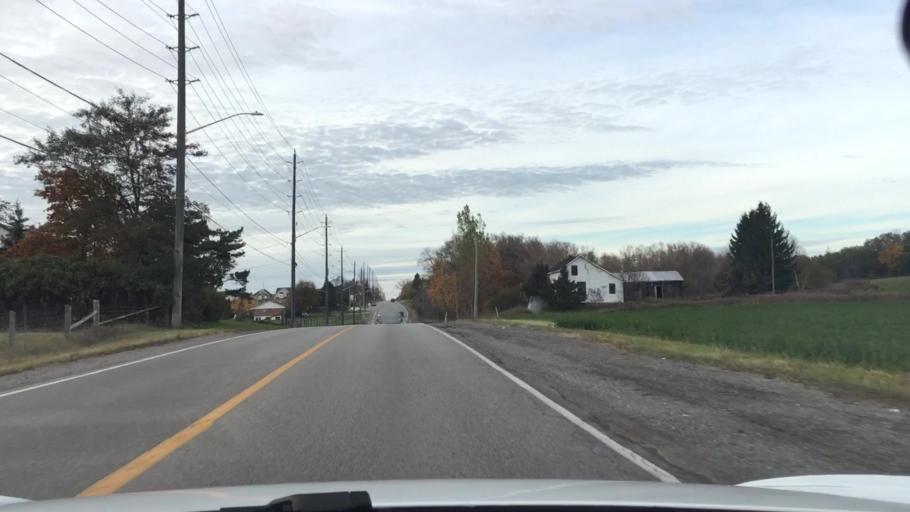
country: CA
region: Ontario
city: Oshawa
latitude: 43.9325
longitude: -78.8247
